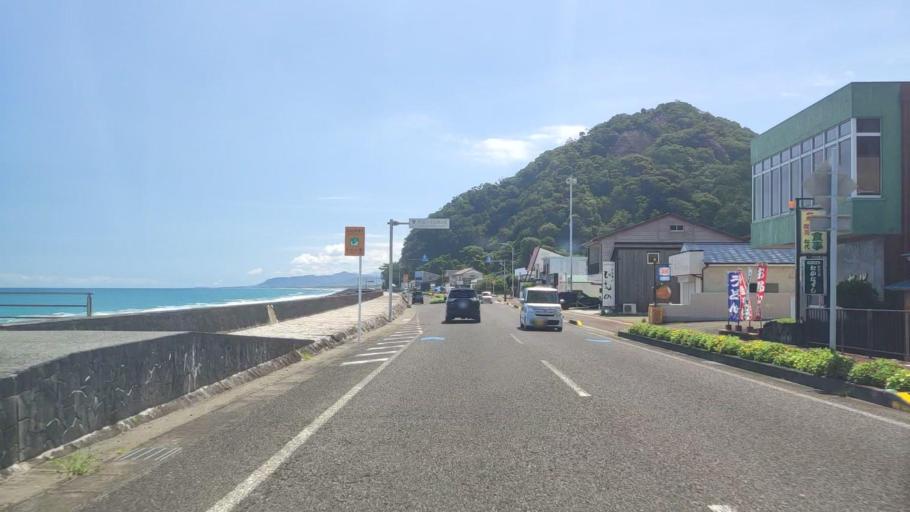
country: JP
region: Wakayama
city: Shingu
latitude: 33.8822
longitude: 136.0961
